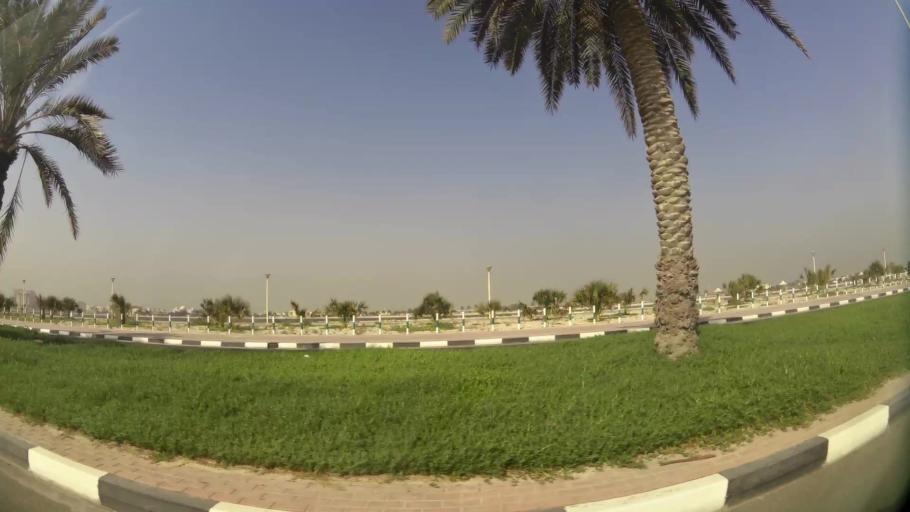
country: AE
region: Ash Shariqah
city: Sharjah
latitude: 25.3069
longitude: 55.3542
